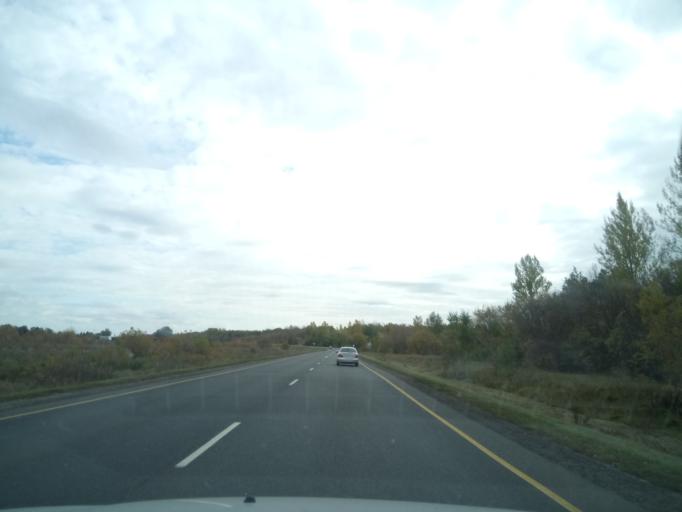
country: RU
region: Nizjnij Novgorod
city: Lukoyanov
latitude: 55.0525
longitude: 44.3737
